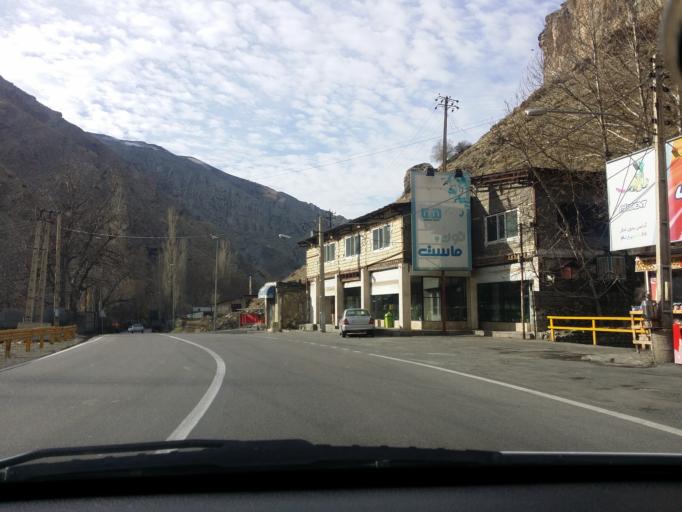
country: IR
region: Alborz
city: Karaj
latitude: 36.0181
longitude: 51.1481
